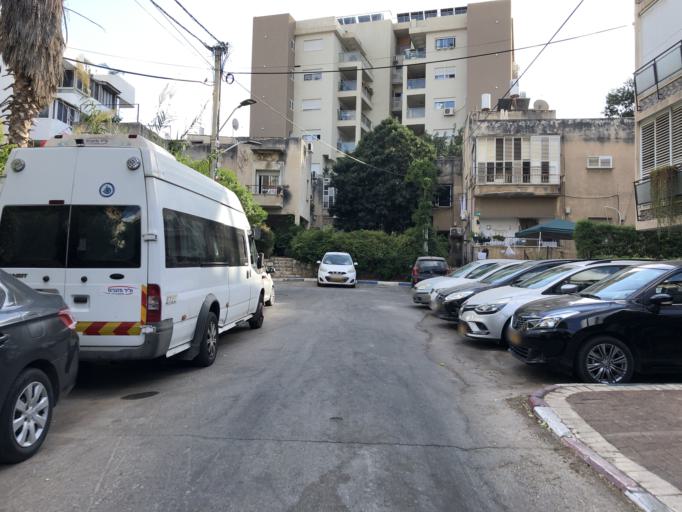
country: IL
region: Tel Aviv
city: Ramat Gan
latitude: 32.0814
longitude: 34.8196
